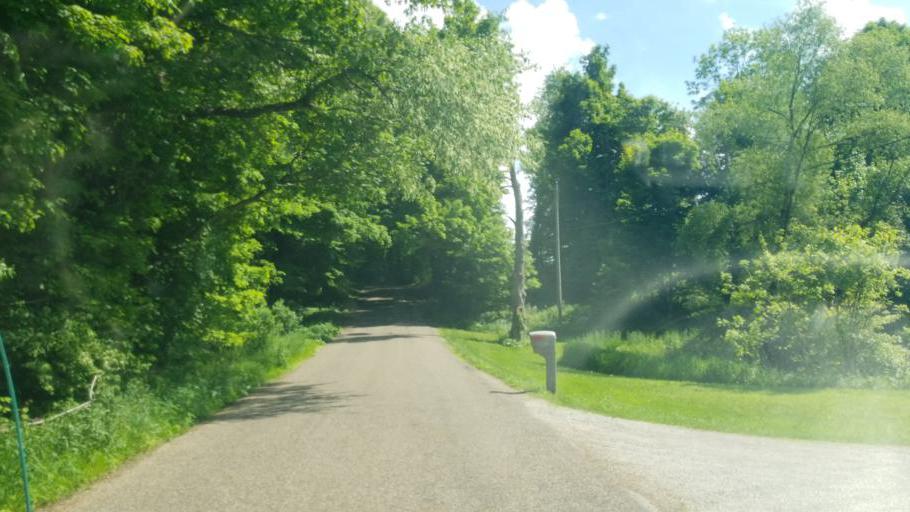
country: US
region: Ohio
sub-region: Sandusky County
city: Bellville
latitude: 40.6492
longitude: -82.5259
